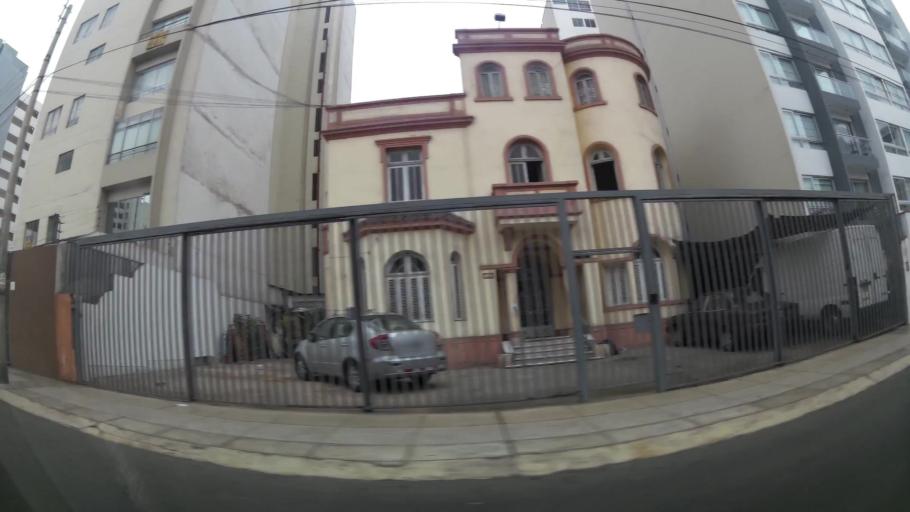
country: PE
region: Lima
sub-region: Lima
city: San Isidro
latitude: -12.1080
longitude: -77.0307
